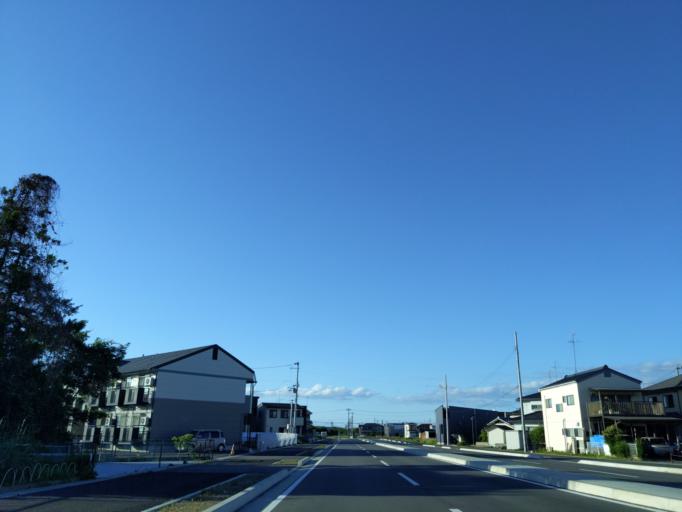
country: JP
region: Fukushima
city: Koriyama
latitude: 37.3912
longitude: 140.4013
